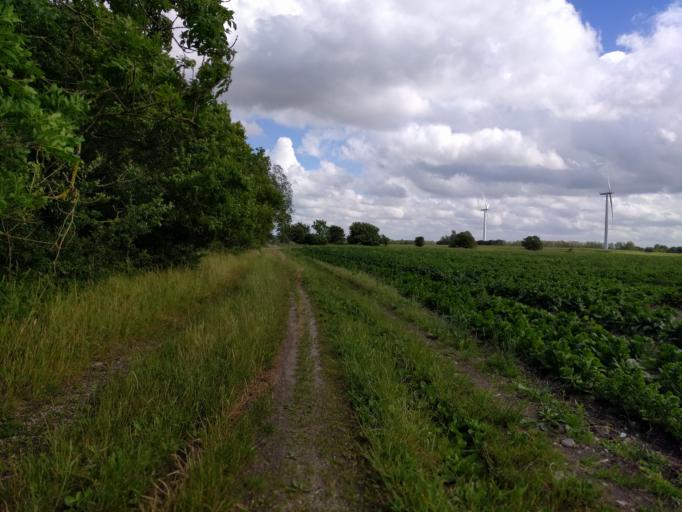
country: DK
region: South Denmark
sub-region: Kerteminde Kommune
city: Munkebo
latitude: 55.4664
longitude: 10.5120
